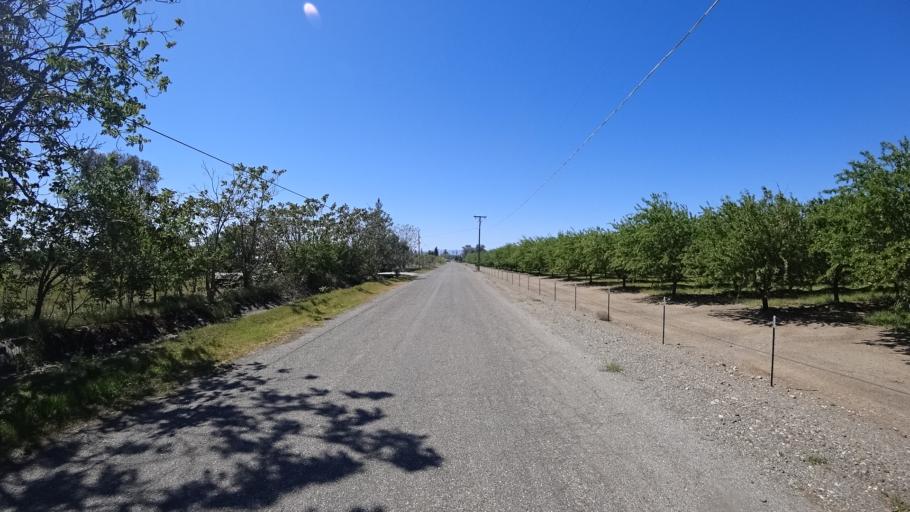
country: US
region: California
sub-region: Glenn County
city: Orland
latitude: 39.7417
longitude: -122.1721
